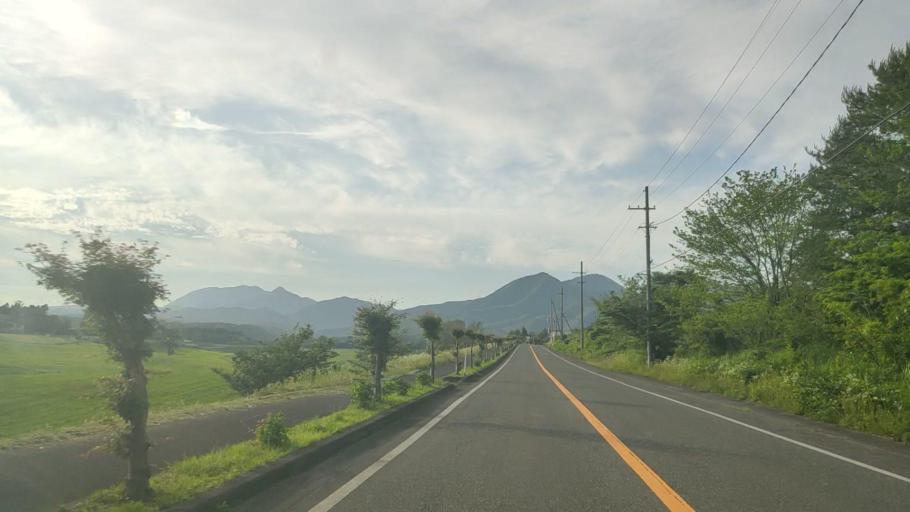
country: JP
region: Tottori
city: Kurayoshi
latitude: 35.2929
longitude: 133.6354
